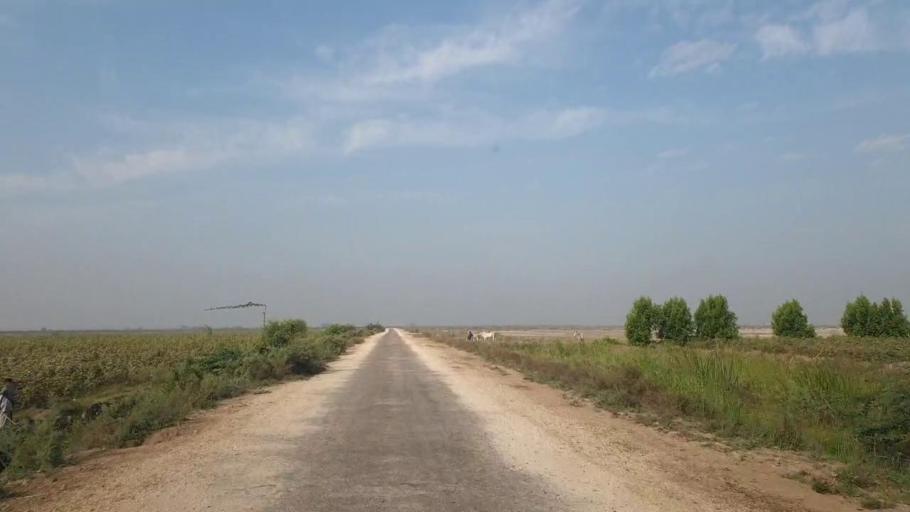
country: PK
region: Sindh
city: Tando Bago
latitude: 24.8445
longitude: 68.9909
